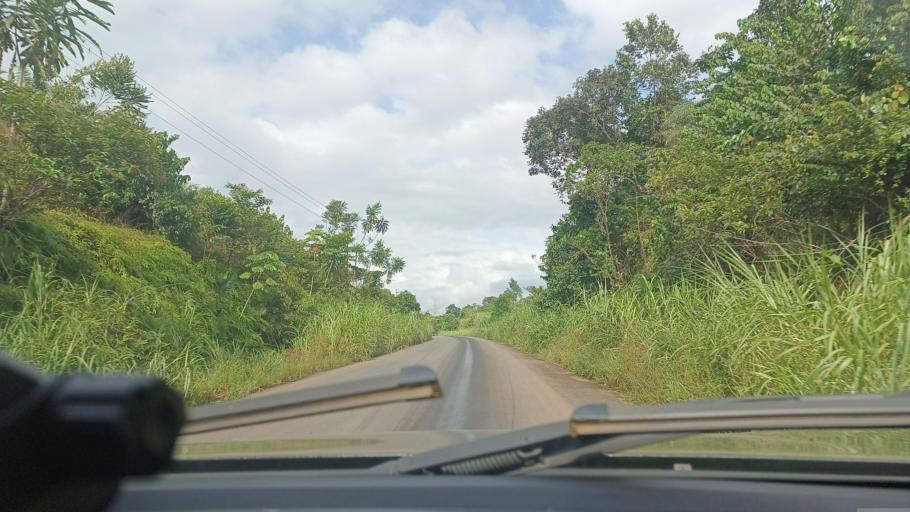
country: LR
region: Bomi
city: Tubmanburg
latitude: 6.7318
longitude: -10.9934
